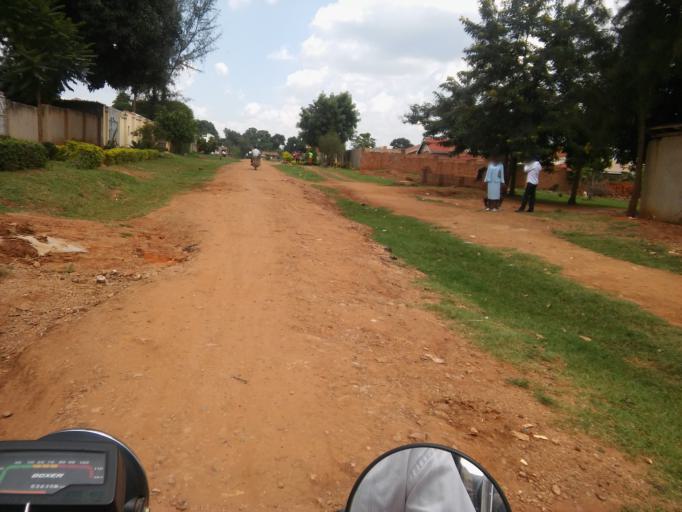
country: UG
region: Eastern Region
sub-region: Mbale District
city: Mbale
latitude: 1.0728
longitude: 34.1710
